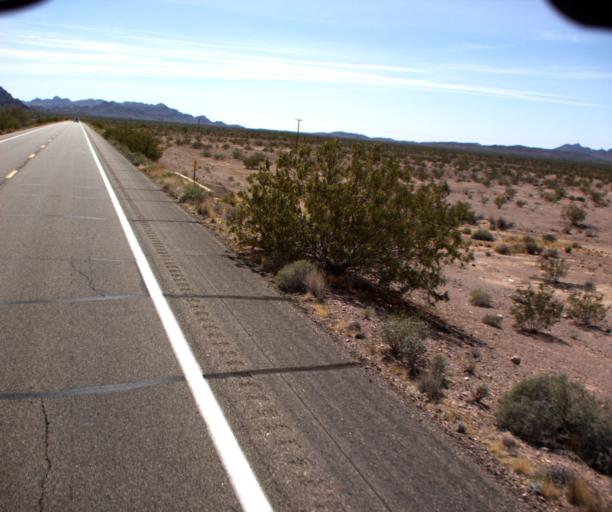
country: US
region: Arizona
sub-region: La Paz County
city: Quartzsite
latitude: 33.3176
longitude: -114.2169
